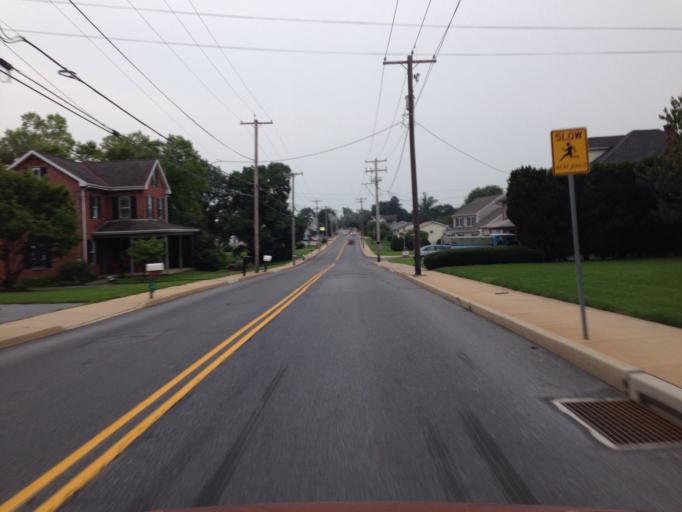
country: US
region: Pennsylvania
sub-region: Lancaster County
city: Ephrata
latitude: 40.1674
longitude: -76.1672
